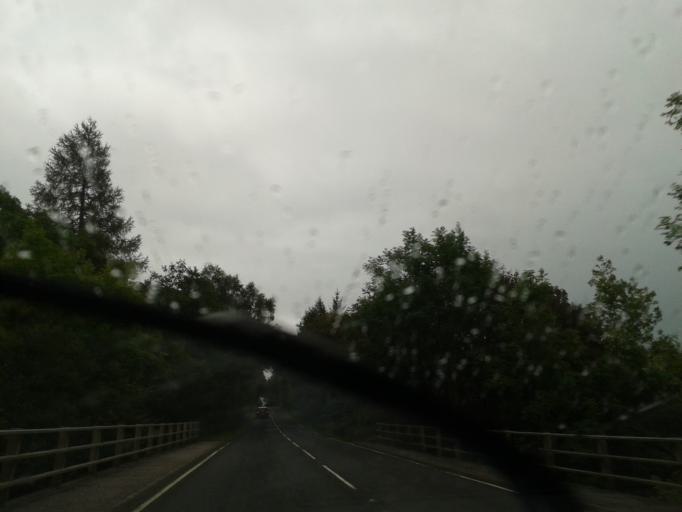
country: GB
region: Scotland
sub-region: Highland
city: Fort William
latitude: 57.2503
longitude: -5.4727
